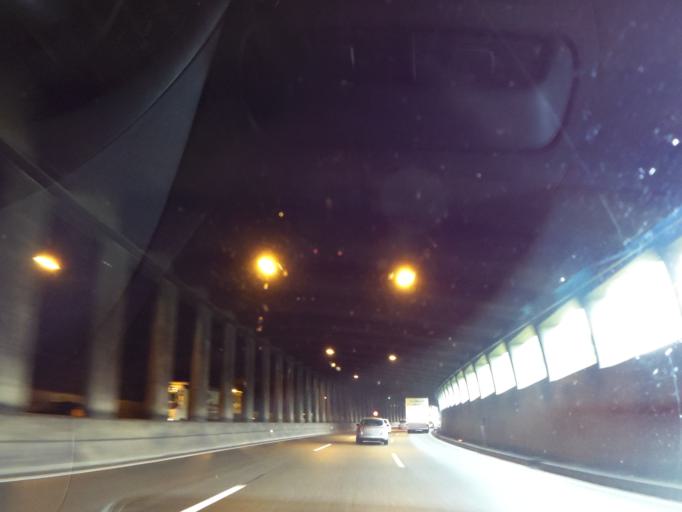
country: AT
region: Tyrol
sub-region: Politischer Bezirk Innsbruck Land
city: Schoenberg im Stubaital
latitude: 47.1890
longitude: 11.4015
